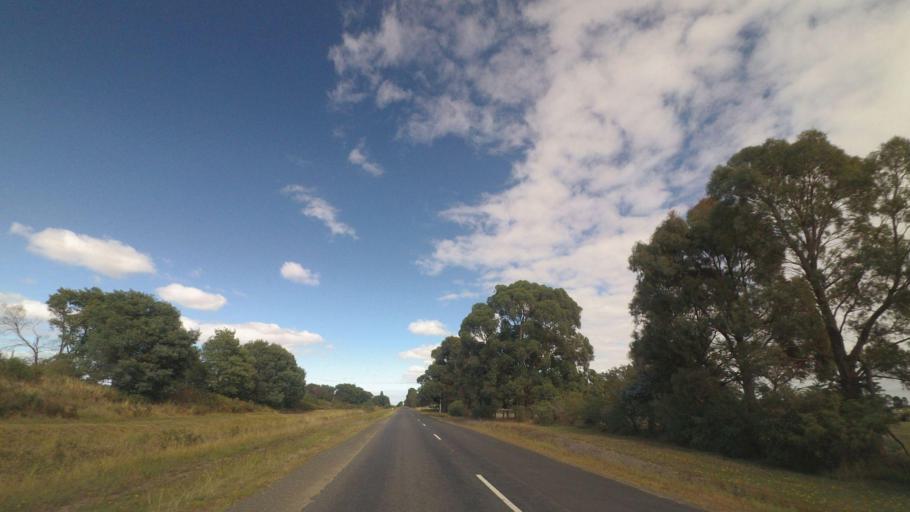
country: AU
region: Victoria
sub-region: Cardinia
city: Pakenham South
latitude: -38.1592
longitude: 145.5425
